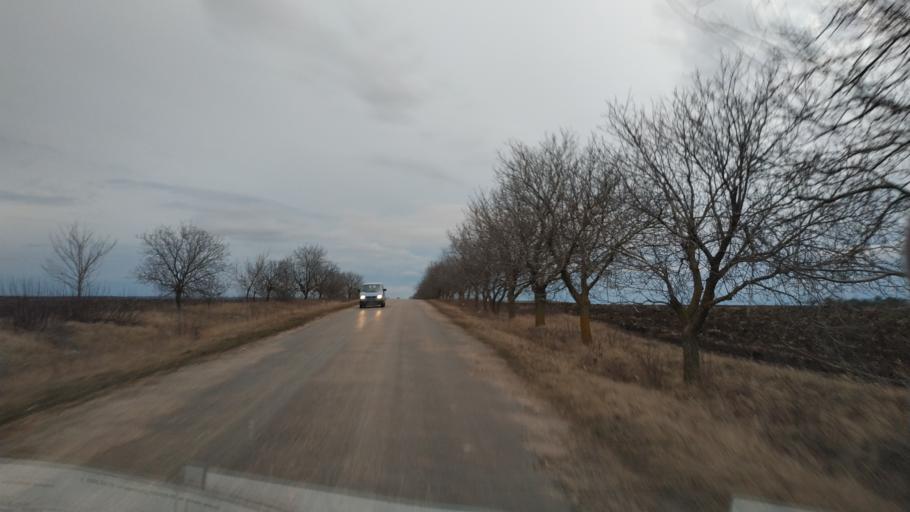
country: MD
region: Causeni
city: Causeni
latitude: 46.5994
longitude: 29.3983
